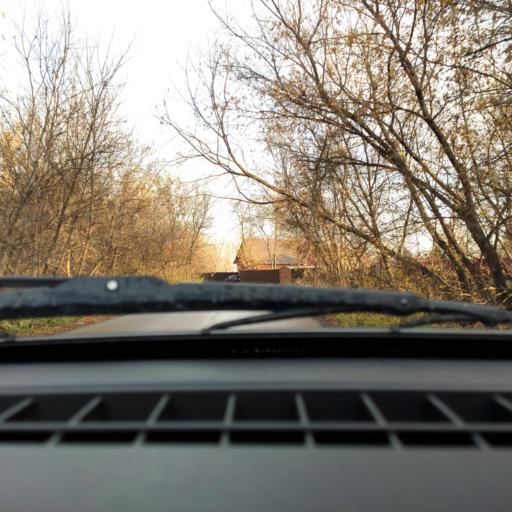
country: RU
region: Bashkortostan
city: Ufa
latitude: 54.8044
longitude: 56.1511
